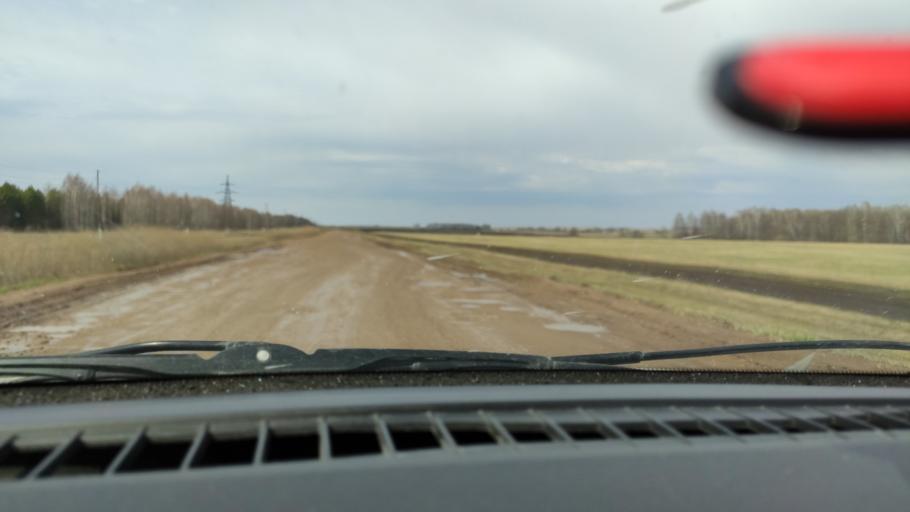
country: RU
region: Bashkortostan
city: Burayevo
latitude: 55.6552
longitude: 55.1702
